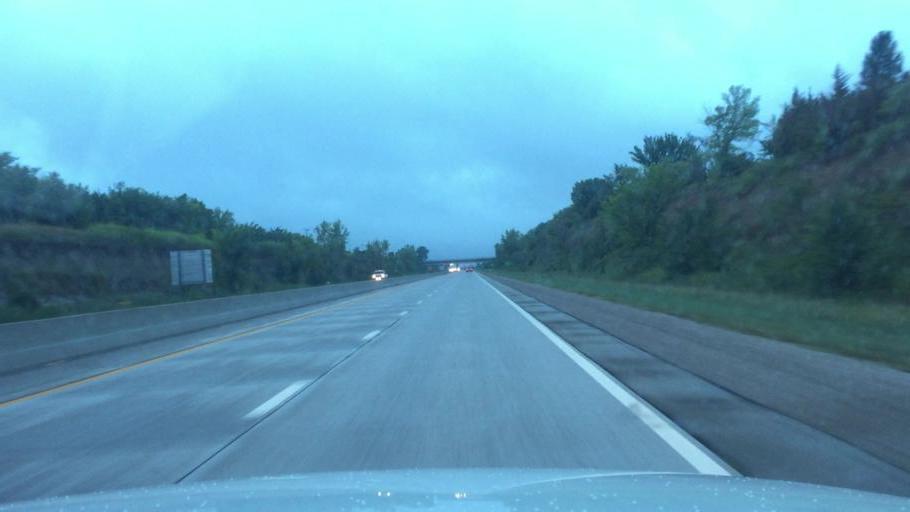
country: US
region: Kansas
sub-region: Neosho County
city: Chanute
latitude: 37.6804
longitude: -95.4796
